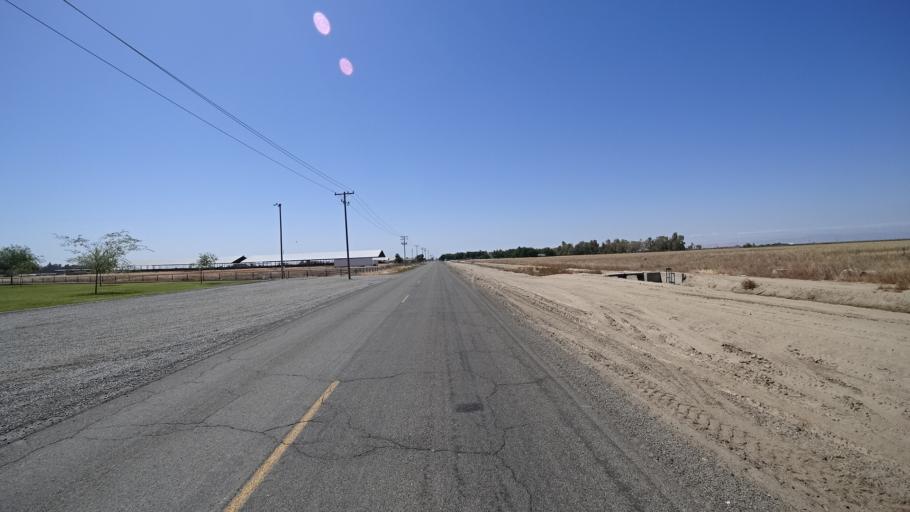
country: US
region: California
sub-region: Kings County
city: Lemoore
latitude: 36.2502
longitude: -119.7987
